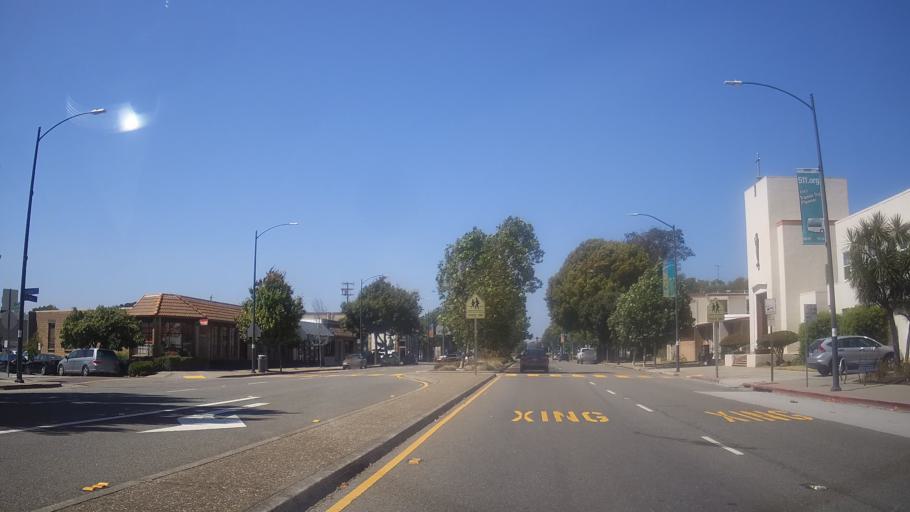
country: US
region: California
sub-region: Contra Costa County
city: El Cerrito
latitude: 37.9185
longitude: -122.3136
